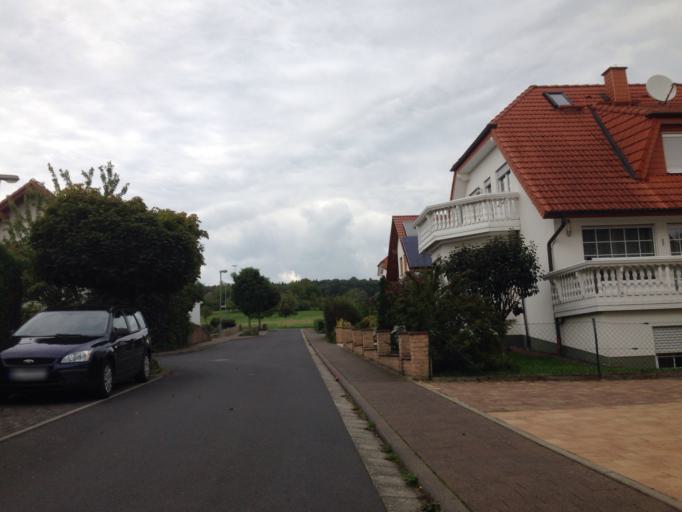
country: DE
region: Hesse
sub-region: Regierungsbezirk Giessen
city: Alten Buseck
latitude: 50.6201
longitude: 8.7624
